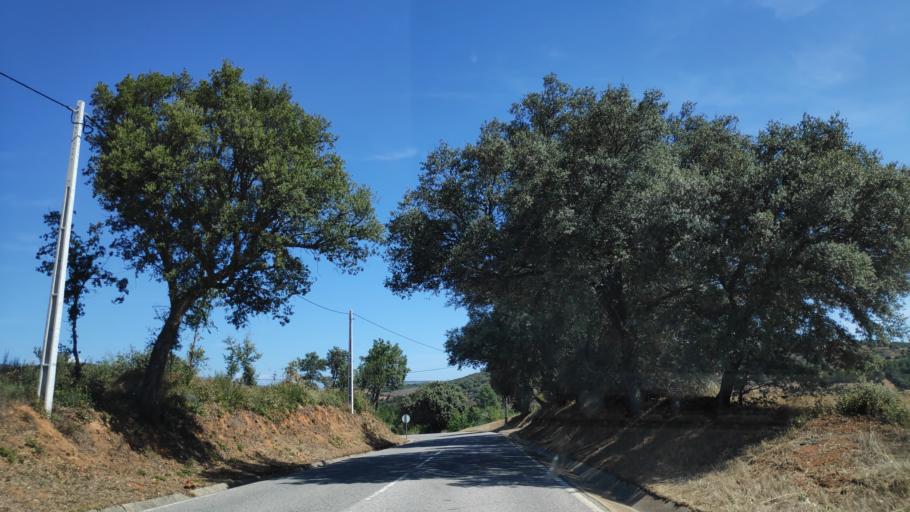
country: PT
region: Braganca
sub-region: Braganca Municipality
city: Braganca
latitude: 41.8260
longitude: -6.7491
